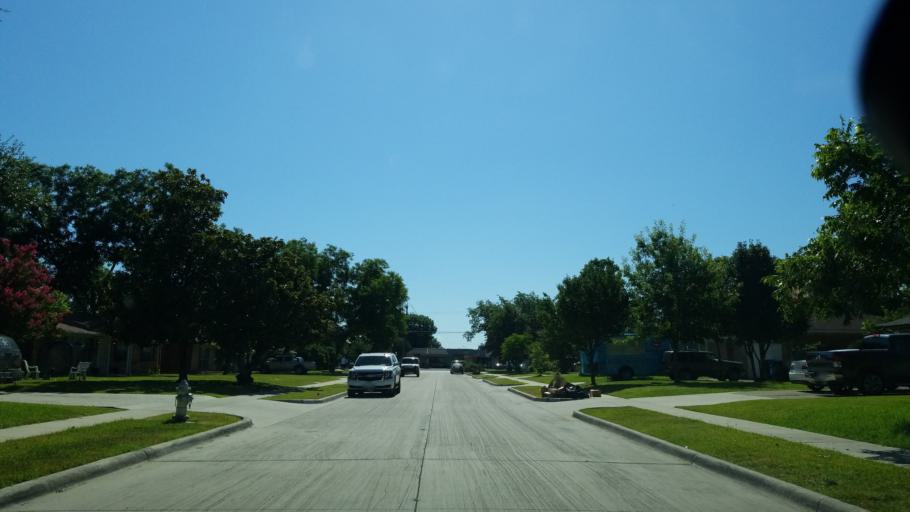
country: US
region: Texas
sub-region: Dallas County
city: Carrollton
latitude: 32.9607
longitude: -96.8917
